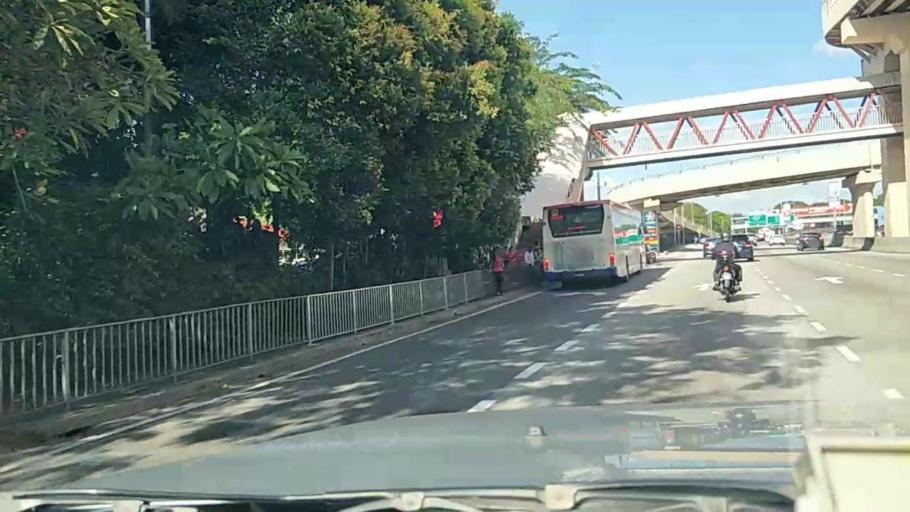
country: MY
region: Selangor
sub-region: Petaling
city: Petaling Jaya
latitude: 3.0740
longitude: 101.6055
